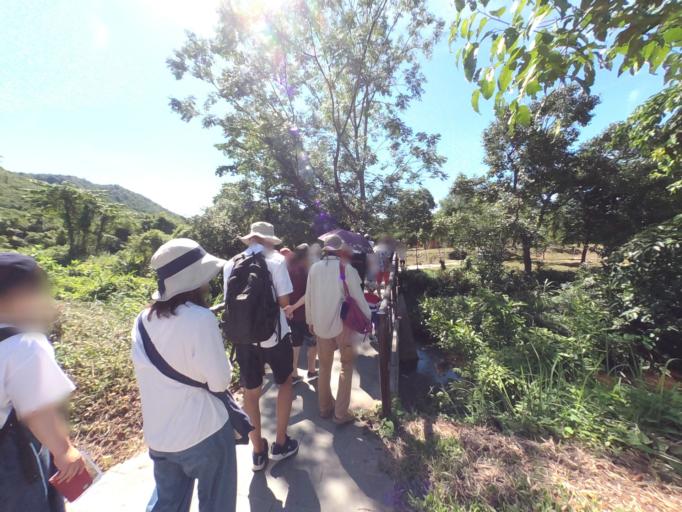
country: VN
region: Quang Nam
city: Dai Loc
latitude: 15.7683
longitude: 108.1205
